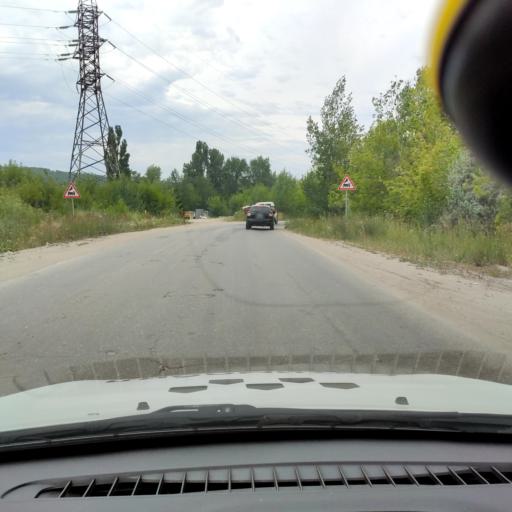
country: RU
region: Samara
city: Zhigulevsk
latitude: 53.4128
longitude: 49.4839
